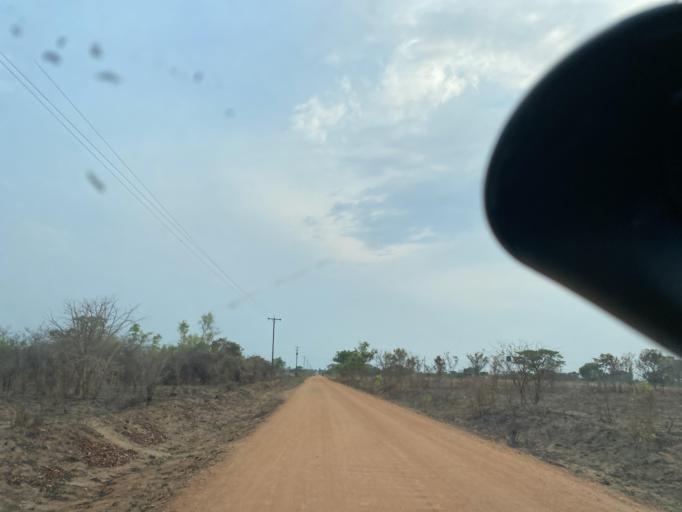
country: ZM
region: Lusaka
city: Chongwe
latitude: -15.2026
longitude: 28.5811
